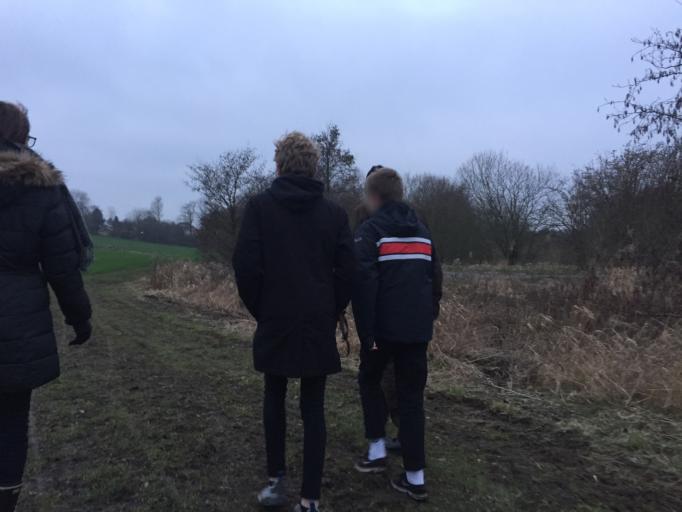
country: DK
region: South Denmark
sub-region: Kolding Kommune
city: Sonder Bjert
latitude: 55.4558
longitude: 9.5641
